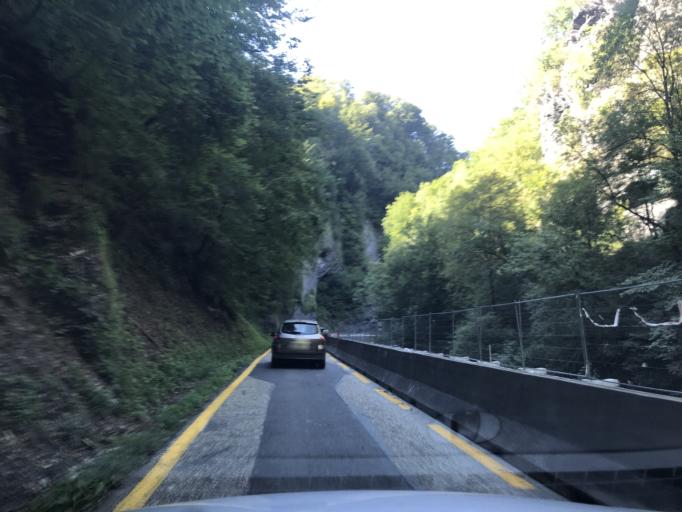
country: FR
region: Rhone-Alpes
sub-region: Departement de la Savoie
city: La Rochette
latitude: 45.4351
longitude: 6.0946
